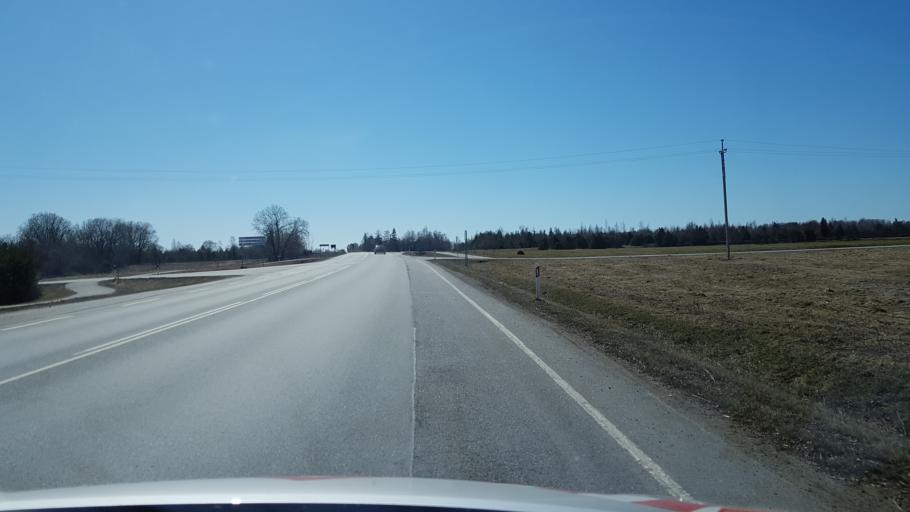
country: EE
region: Laeaene-Virumaa
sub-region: Viru-Nigula vald
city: Kunda
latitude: 59.4815
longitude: 26.4896
